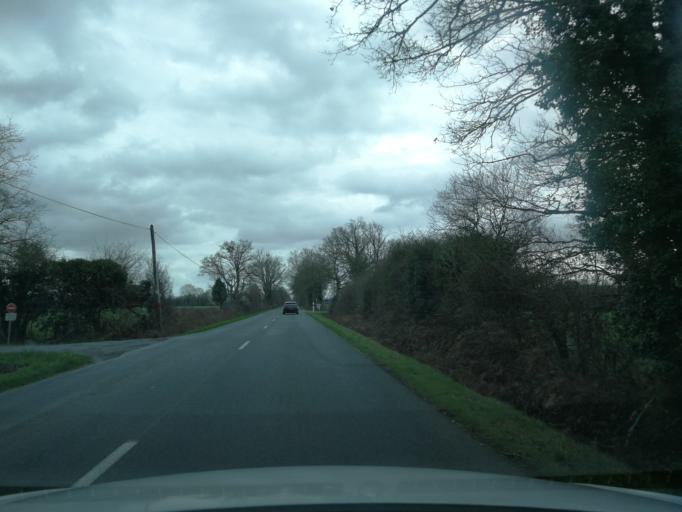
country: FR
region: Pays de la Loire
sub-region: Departement de la Loire-Atlantique
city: Montbert
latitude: 47.0186
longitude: -1.4869
